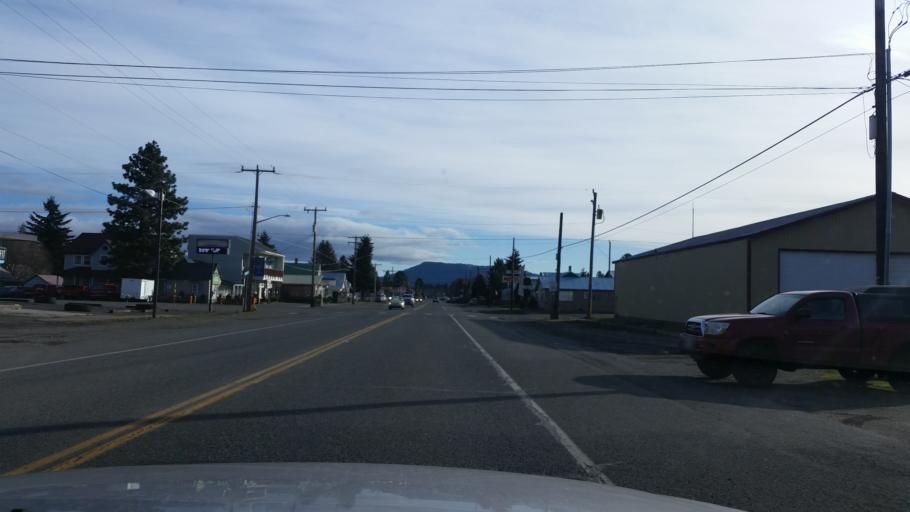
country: US
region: Washington
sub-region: Kittitas County
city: Cle Elum
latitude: 47.1932
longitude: -120.9248
